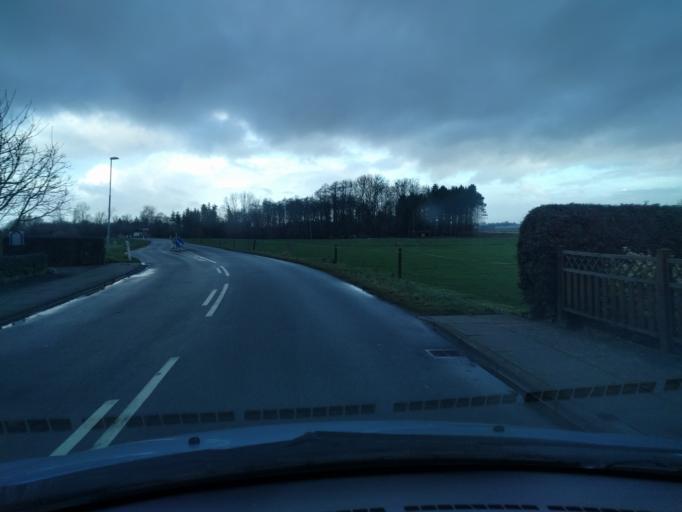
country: DK
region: South Denmark
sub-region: Kerteminde Kommune
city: Langeskov
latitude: 55.3653
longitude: 10.5871
